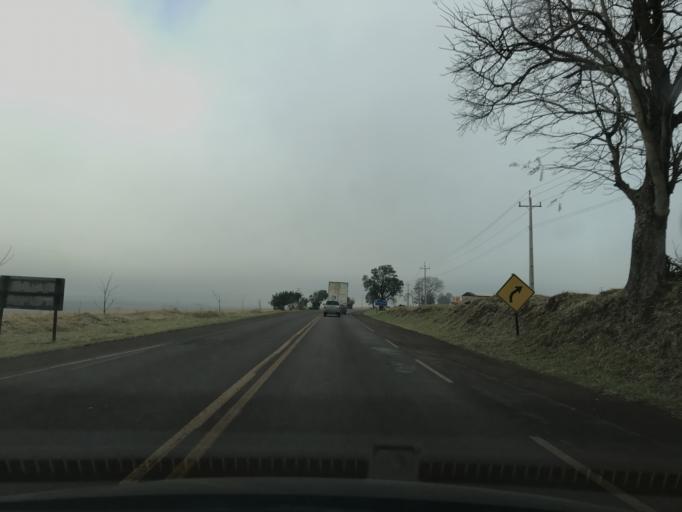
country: BR
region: Parana
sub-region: Toledo
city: Toledo
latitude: -24.6674
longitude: -53.6983
